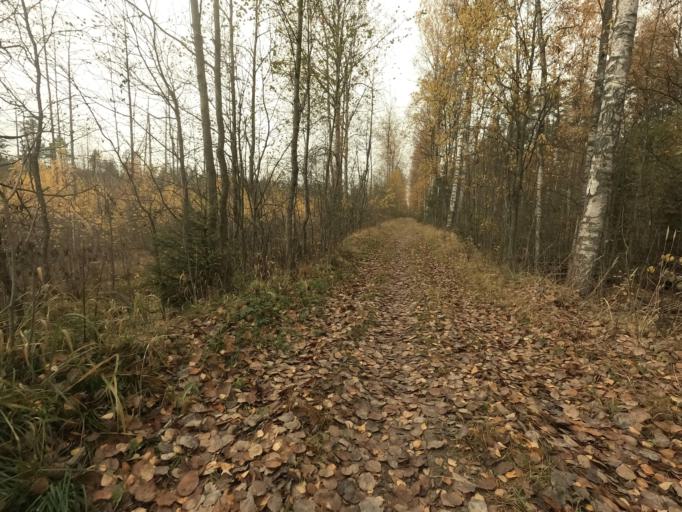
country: RU
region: Leningrad
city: Pavlovo
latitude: 59.7936
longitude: 30.8807
